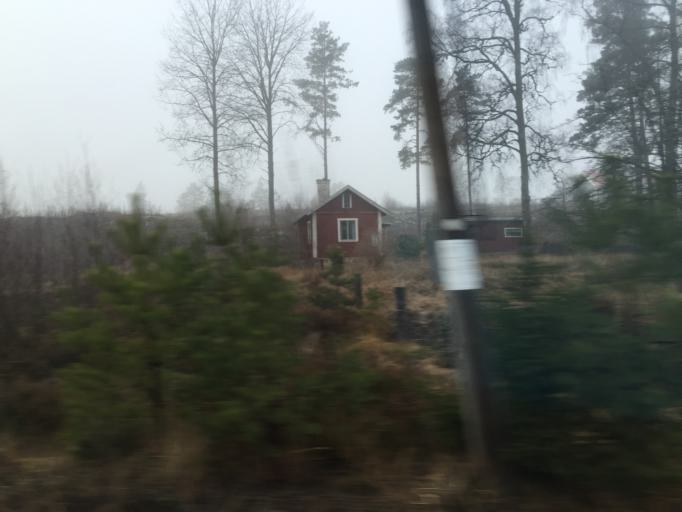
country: SE
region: Stockholm
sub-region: Nynashamns Kommun
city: Osmo
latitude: 59.0583
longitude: 17.8708
